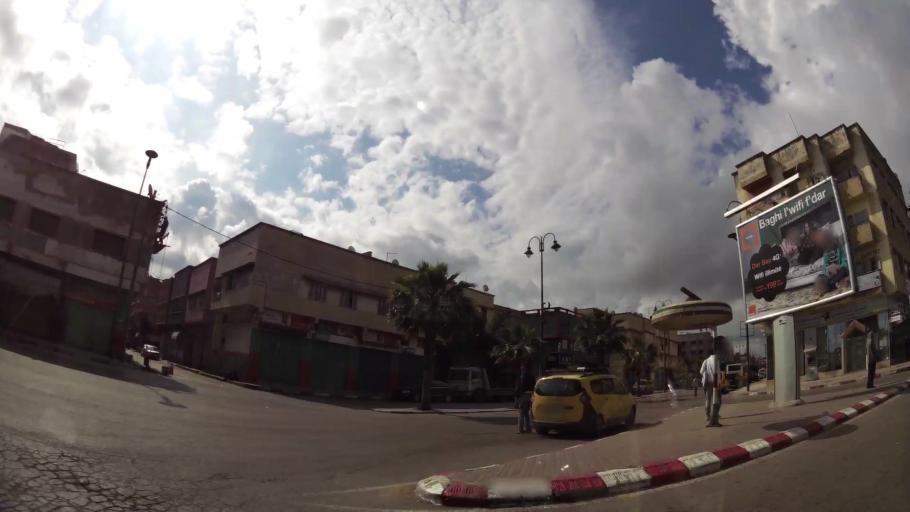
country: MA
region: Gharb-Chrarda-Beni Hssen
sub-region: Kenitra Province
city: Kenitra
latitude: 34.2688
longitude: -6.5612
